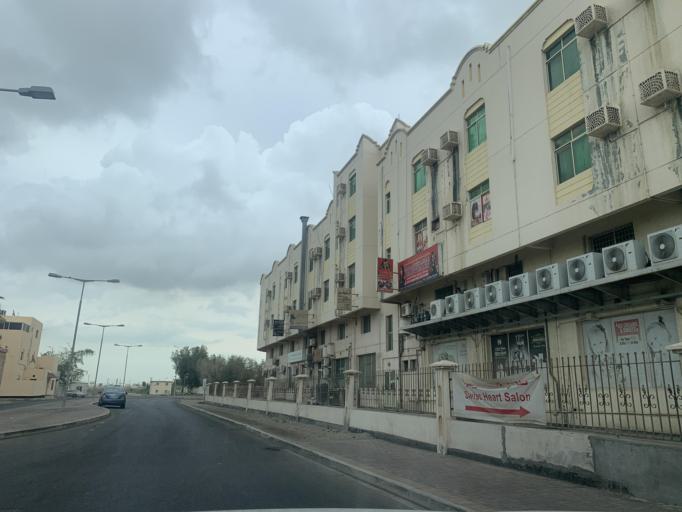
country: BH
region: Muharraq
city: Al Hadd
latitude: 26.2747
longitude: 50.6451
